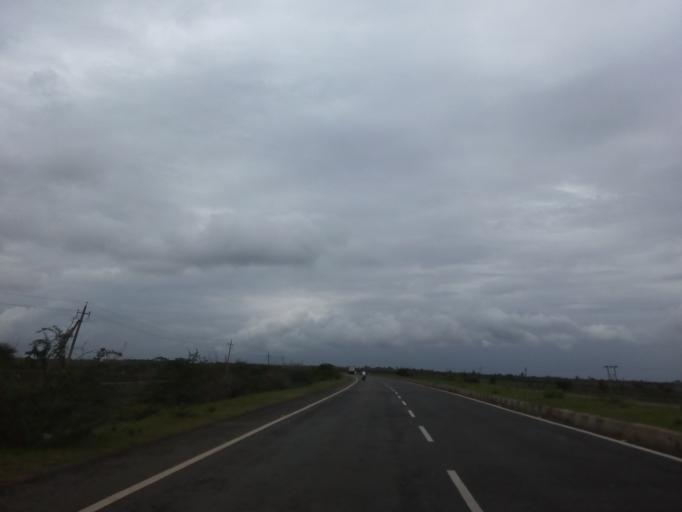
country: IN
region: Karnataka
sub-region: Haveri
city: Ranibennur
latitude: 14.5968
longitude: 75.6311
